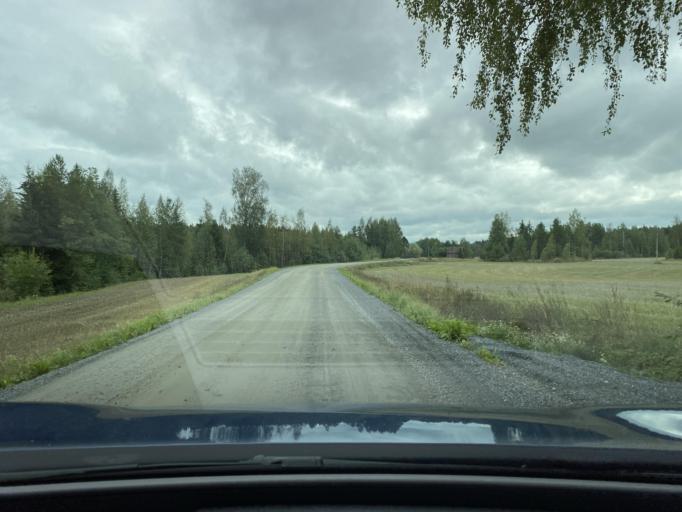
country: FI
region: Pirkanmaa
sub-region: Lounais-Pirkanmaa
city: Vammala
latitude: 61.2696
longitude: 22.9762
